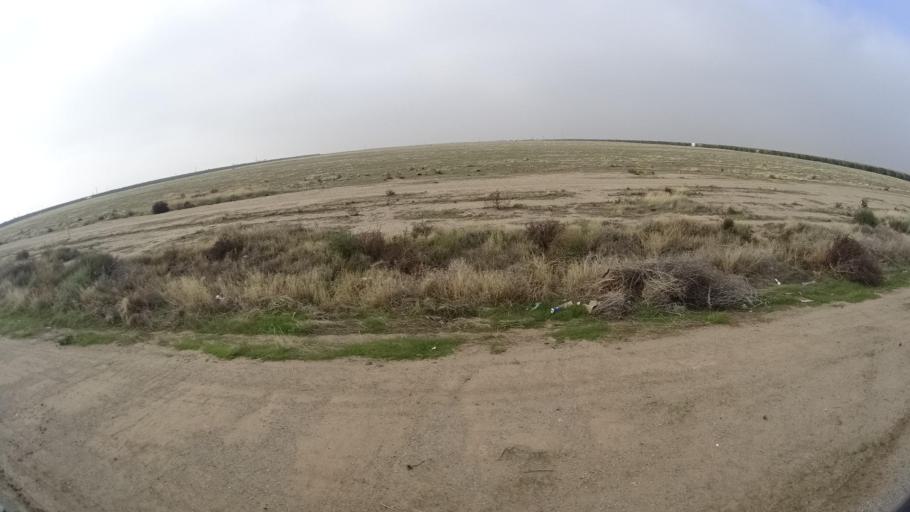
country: US
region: California
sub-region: Kern County
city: Maricopa
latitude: 35.0602
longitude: -119.3137
